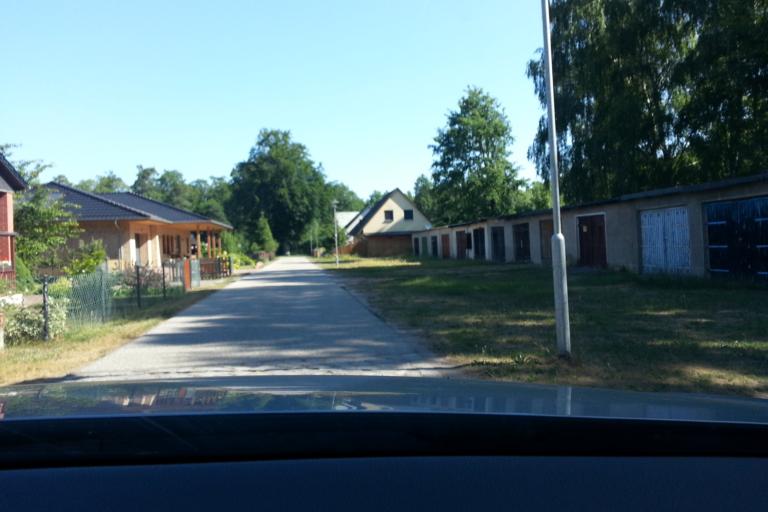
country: DE
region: Mecklenburg-Vorpommern
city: Torgelow
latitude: 53.6410
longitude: 14.0401
